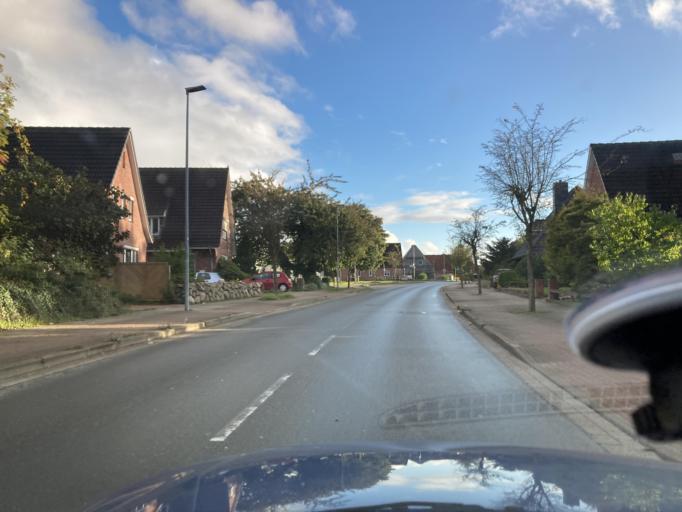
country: DE
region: Schleswig-Holstein
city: Heide
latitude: 54.2035
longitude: 9.1060
